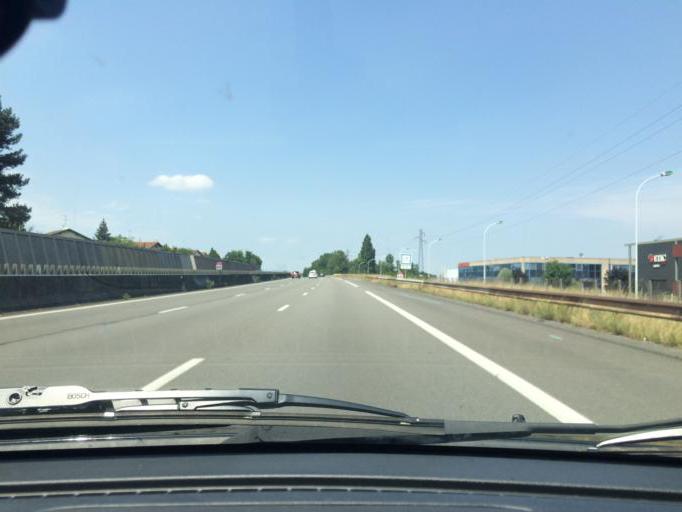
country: FR
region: Rhone-Alpes
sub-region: Departement du Rhone
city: Villefranche-sur-Saone
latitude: 45.9917
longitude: 4.7371
